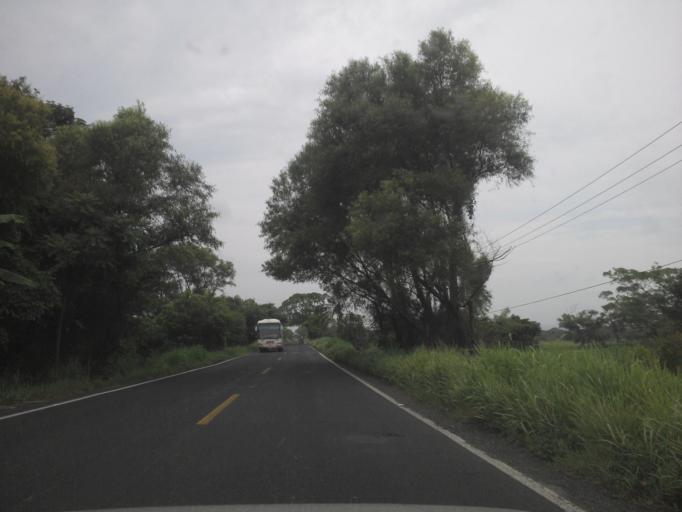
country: MX
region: Veracruz
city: Nautla
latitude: 20.2184
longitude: -96.7851
